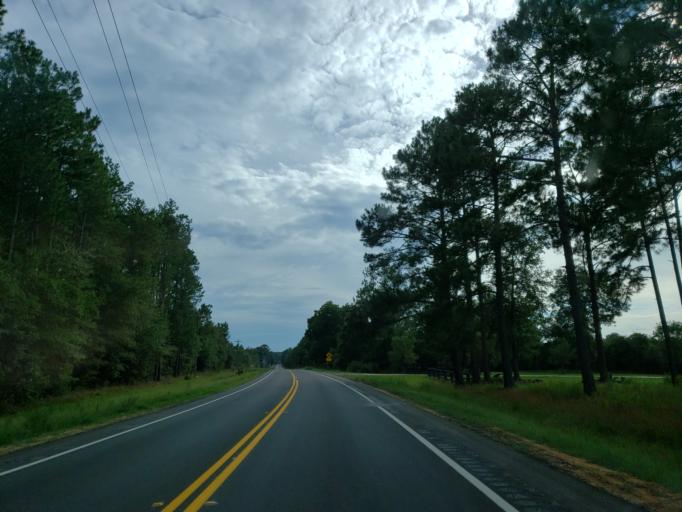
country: US
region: Georgia
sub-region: Irwin County
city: Ocilla
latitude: 31.5740
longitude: -83.3034
